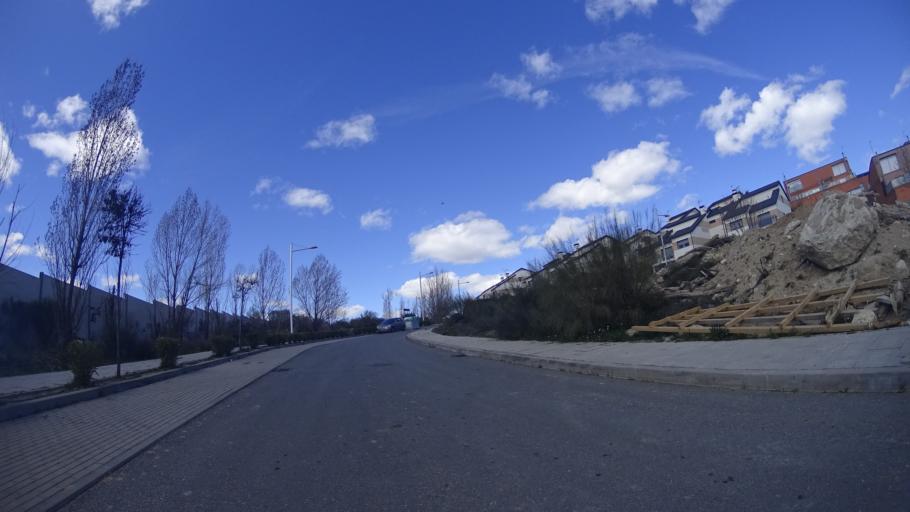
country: ES
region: Madrid
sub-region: Provincia de Madrid
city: Torrelodones
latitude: 40.5635
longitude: -3.9221
